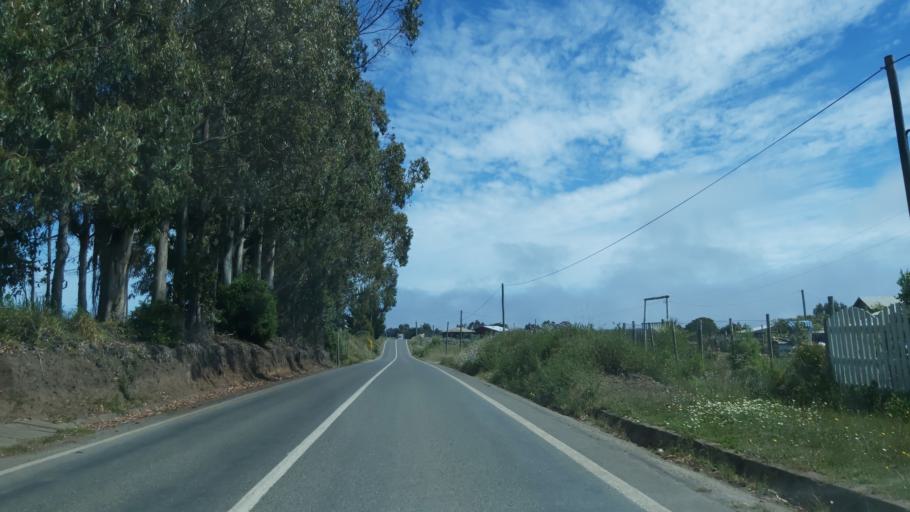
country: CL
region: Maule
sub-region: Provincia de Talca
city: Constitucion
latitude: -35.5799
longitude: -72.6013
